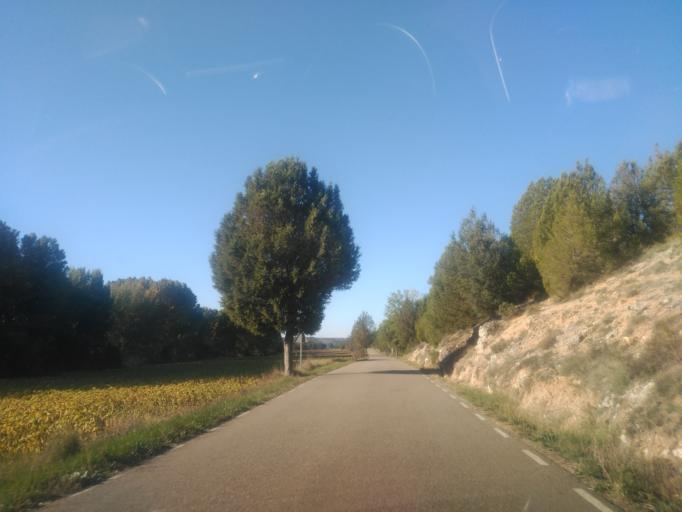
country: ES
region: Castille and Leon
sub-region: Provincia de Burgos
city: Brazacorta
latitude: 41.7084
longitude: -3.3882
